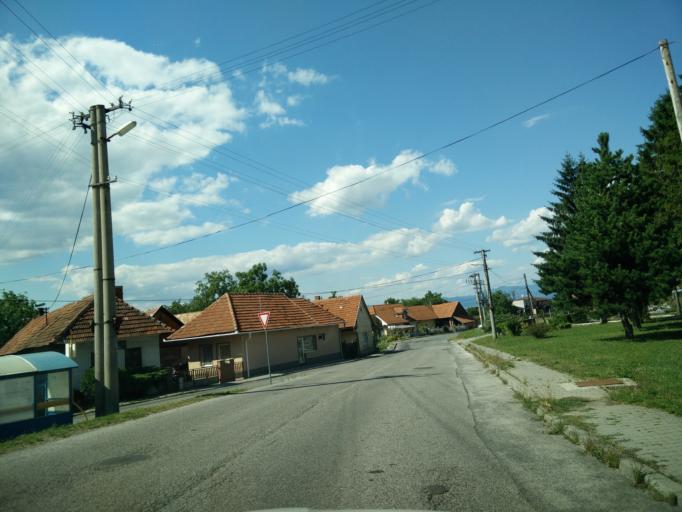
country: SK
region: Nitriansky
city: Prievidza
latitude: 48.7326
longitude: 18.6204
